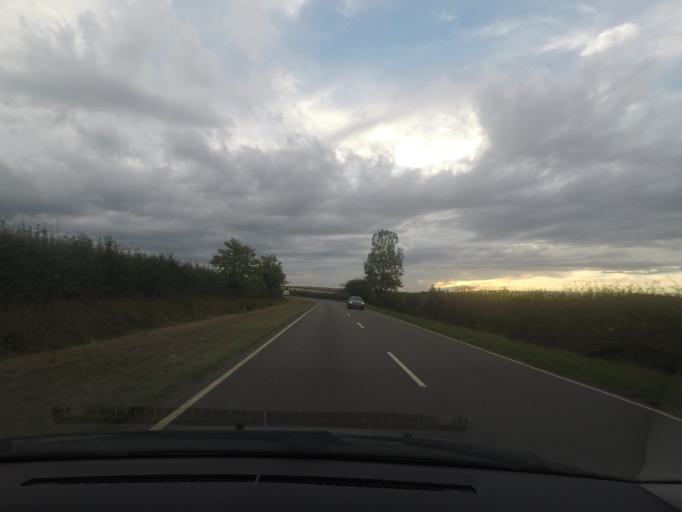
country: GB
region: England
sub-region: Lincolnshire
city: Tetney
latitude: 53.4369
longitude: -0.0565
